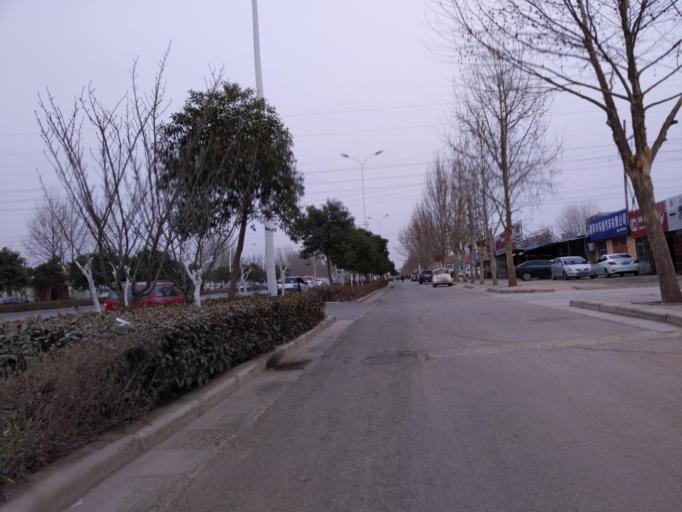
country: CN
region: Henan Sheng
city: Zhongyuanlu
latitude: 35.7547
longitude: 115.0936
